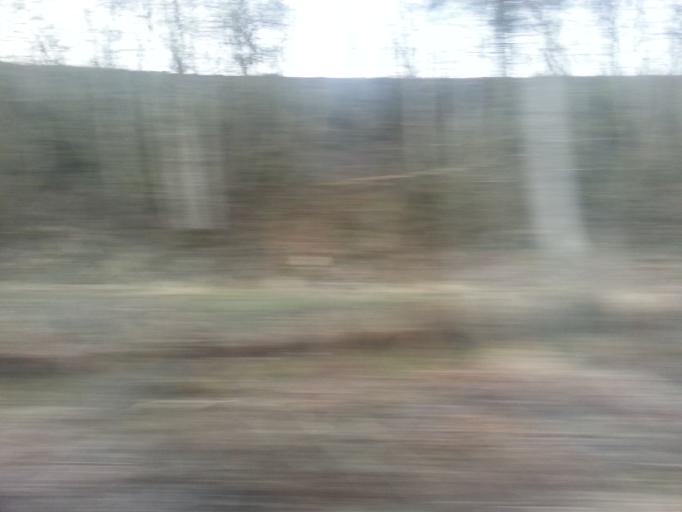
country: NO
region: Sor-Trondelag
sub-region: Melhus
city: Lundamo
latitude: 63.1639
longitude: 10.2973
